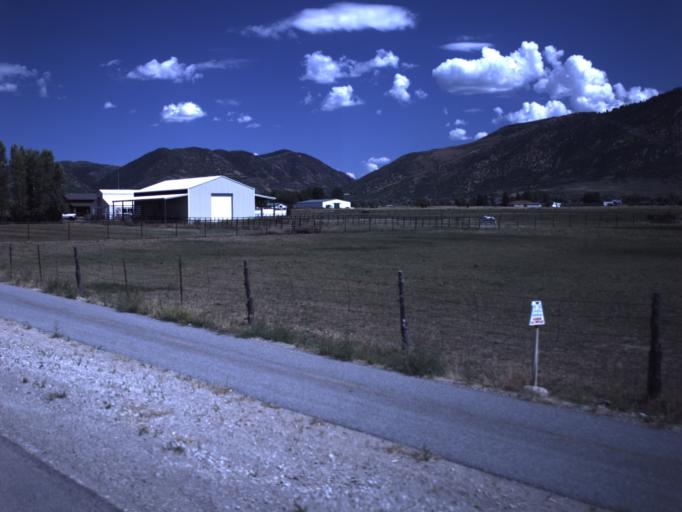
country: US
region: Utah
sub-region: Summit County
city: Oakley
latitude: 40.6998
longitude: -111.2810
